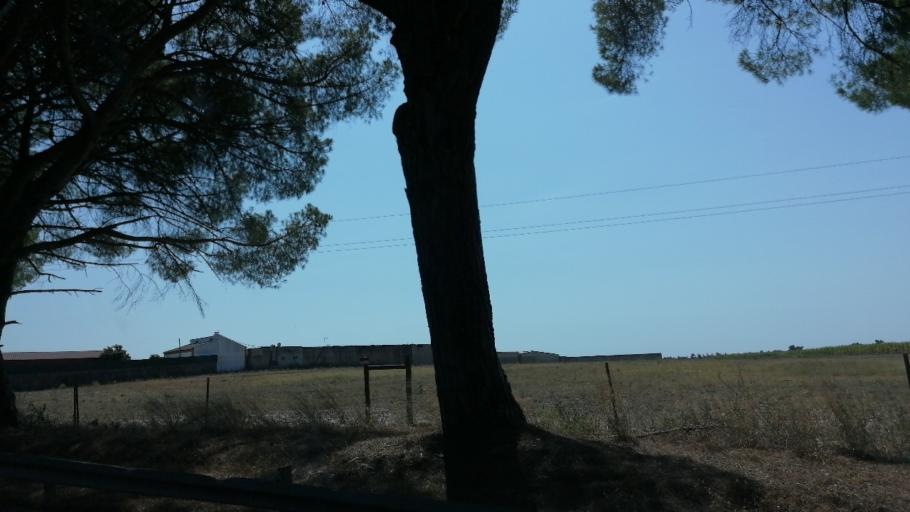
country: PT
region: Evora
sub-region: Vendas Novas
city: Vendas Novas
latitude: 38.6982
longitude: -8.6115
